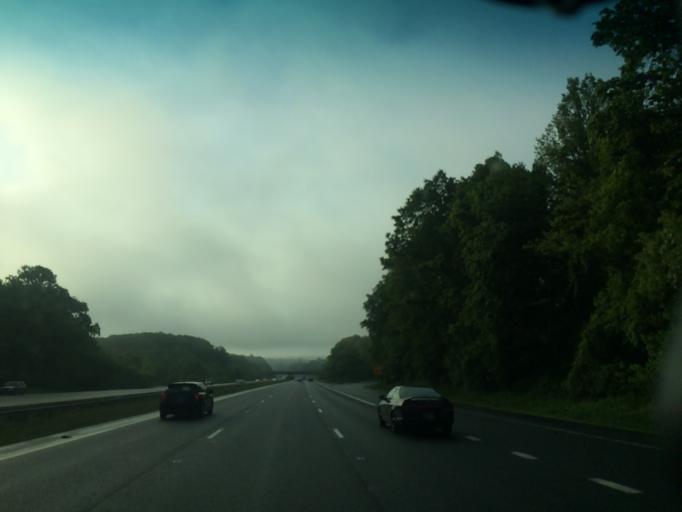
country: US
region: Maryland
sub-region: Carroll County
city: Mount Airy
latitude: 39.3446
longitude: -77.0780
